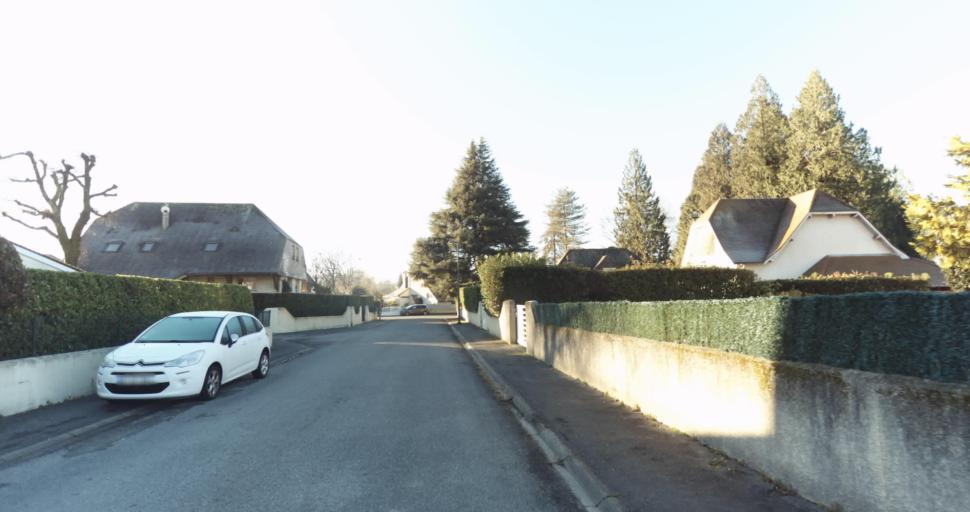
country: FR
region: Aquitaine
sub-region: Departement des Pyrenees-Atlantiques
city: Morlaas
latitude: 43.3294
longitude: -0.2828
